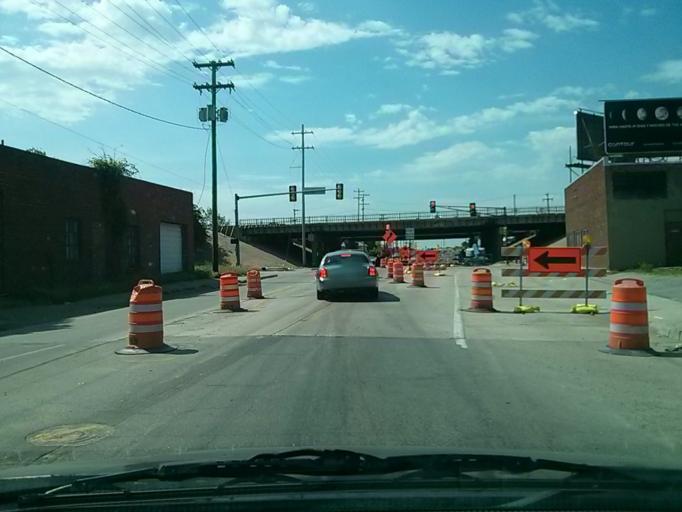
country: US
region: Oklahoma
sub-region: Tulsa County
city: Tulsa
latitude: 36.1603
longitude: -95.9757
